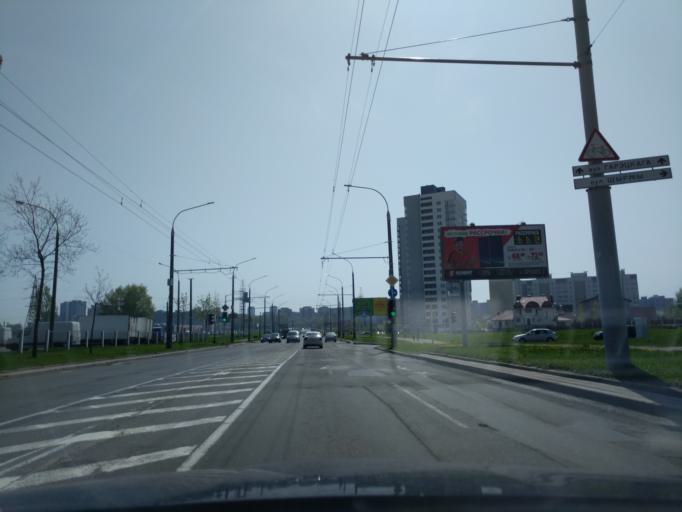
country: BY
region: Minsk
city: Novoye Medvezhino
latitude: 53.8784
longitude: 27.4586
